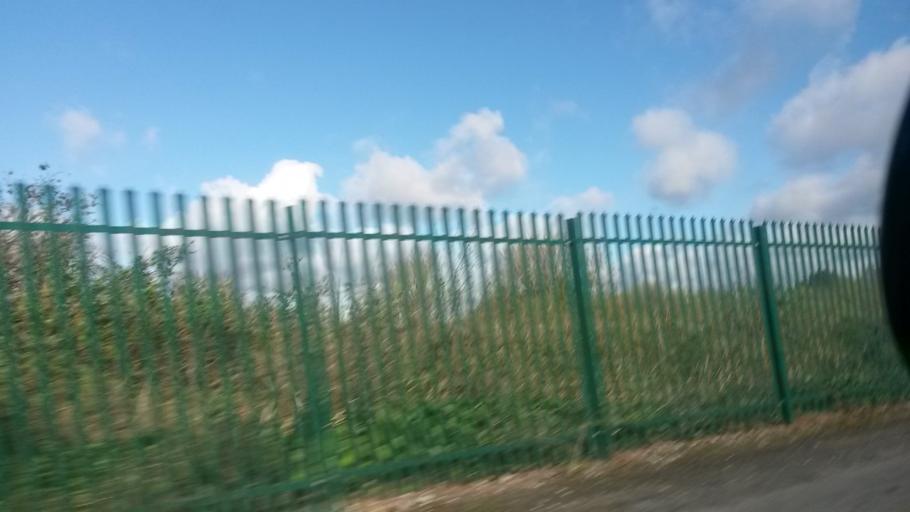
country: IE
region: Munster
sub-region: County Cork
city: Passage West
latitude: 51.8722
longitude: -8.3231
